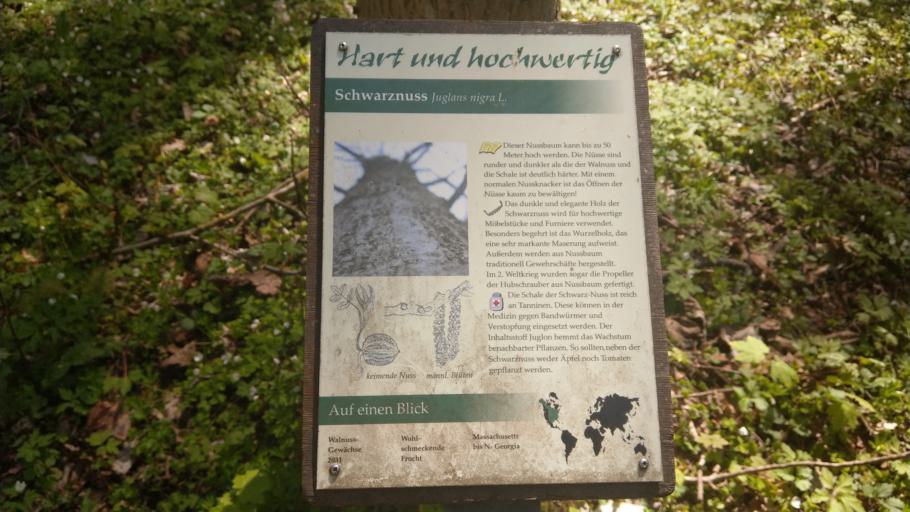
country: DE
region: Baden-Wuerttemberg
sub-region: Regierungsbezirk Stuttgart
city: Kohlberg
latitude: 48.5613
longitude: 9.3131
